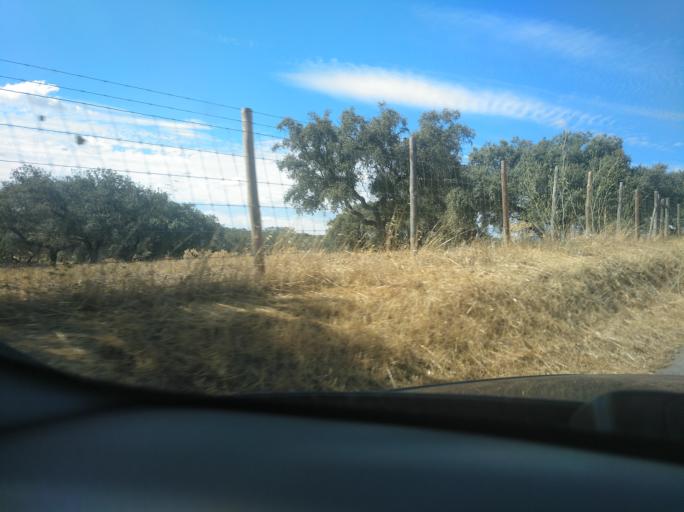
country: ES
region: Extremadura
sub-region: Provincia de Badajoz
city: La Codosera
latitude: 39.1263
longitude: -7.1562
